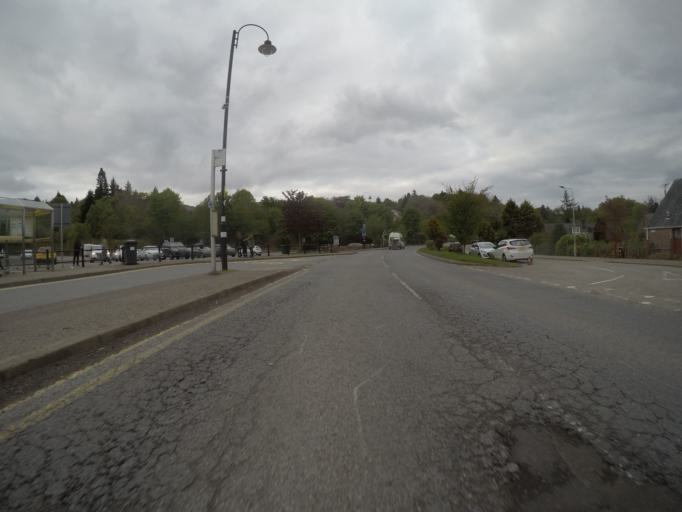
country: GB
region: Scotland
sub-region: Highland
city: Spean Bridge
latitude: 57.1464
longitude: -4.6813
